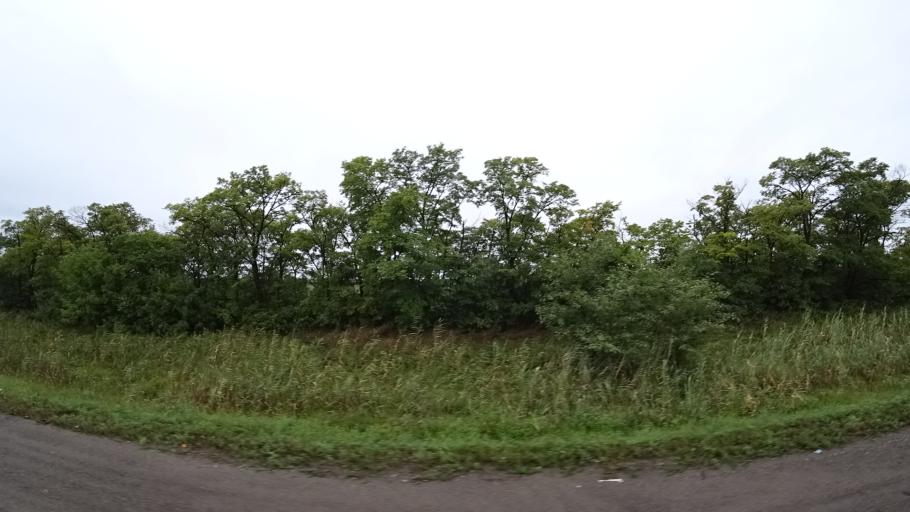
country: RU
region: Primorskiy
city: Monastyrishche
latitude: 44.2286
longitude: 132.4536
